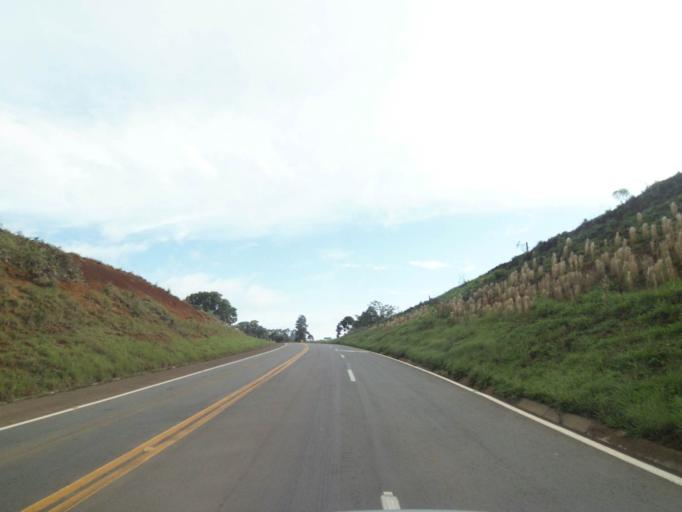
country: BR
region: Rio Grande do Sul
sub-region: Lagoa Vermelha
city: Lagoa Vermelha
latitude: -28.2131
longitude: -51.5473
